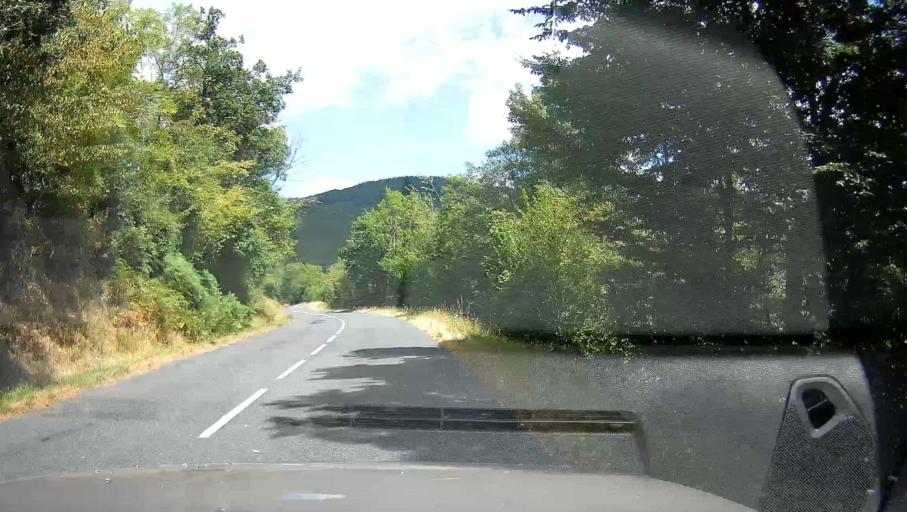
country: FR
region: Rhone-Alpes
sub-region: Departement du Rhone
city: Cogny
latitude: 46.0136
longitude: 4.5823
